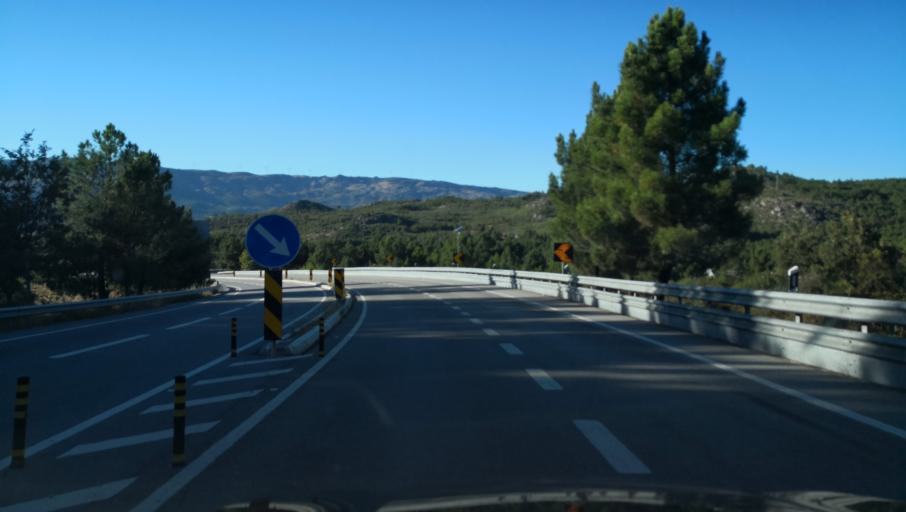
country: PT
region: Vila Real
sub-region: Vila Real
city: Vila Real
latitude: 41.3279
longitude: -7.6722
